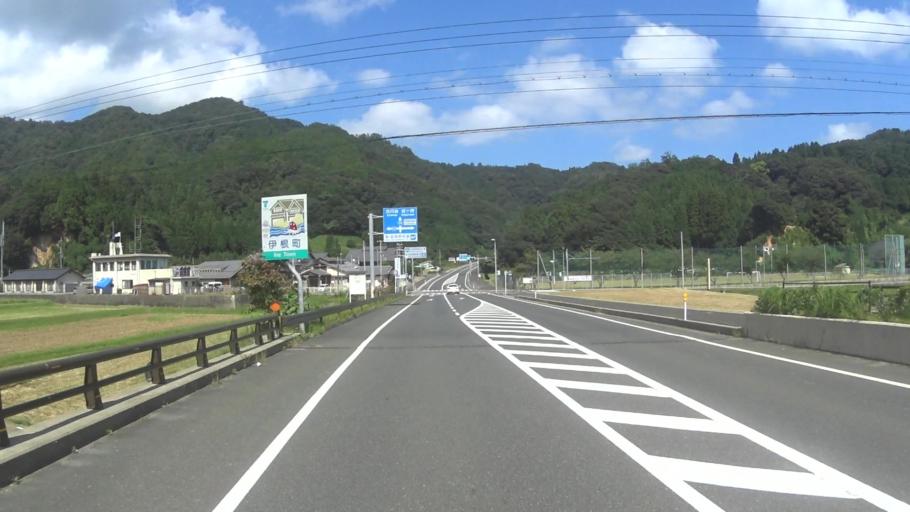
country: JP
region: Kyoto
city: Miyazu
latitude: 35.6732
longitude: 135.2721
